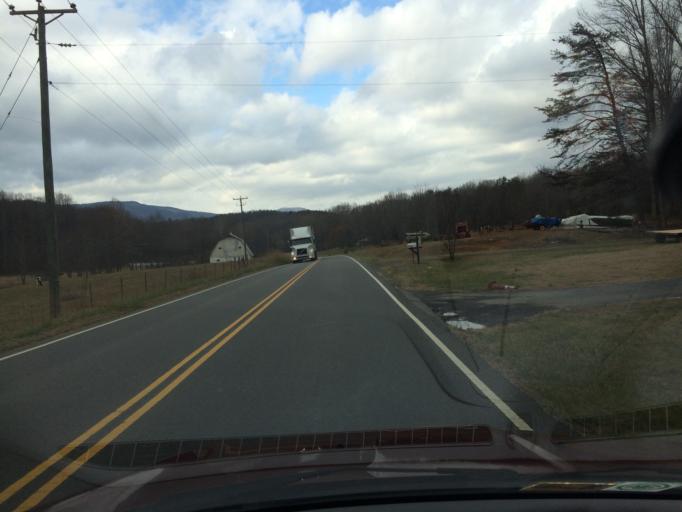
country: US
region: Virginia
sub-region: Patrick County
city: Stuart
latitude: 36.7467
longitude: -80.2636
